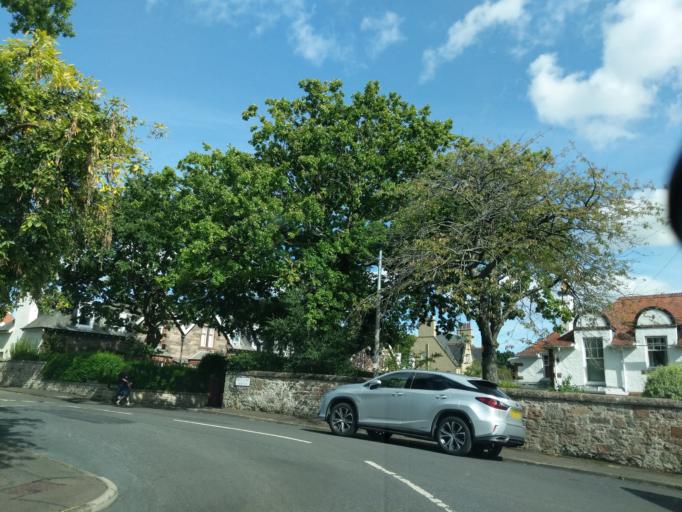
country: GB
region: Scotland
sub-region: Edinburgh
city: Colinton
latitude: 55.9089
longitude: -3.2602
